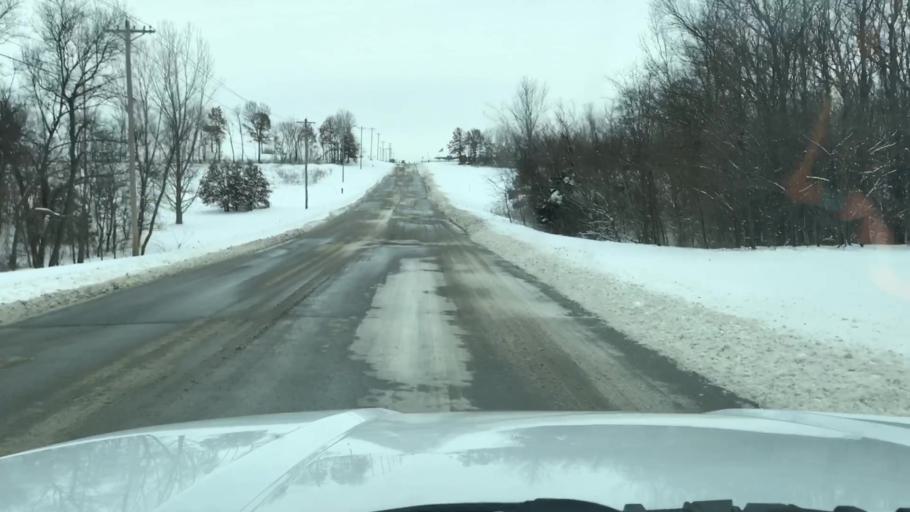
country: US
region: Missouri
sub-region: Clinton County
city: Cameron
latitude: 39.7466
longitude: -94.2153
